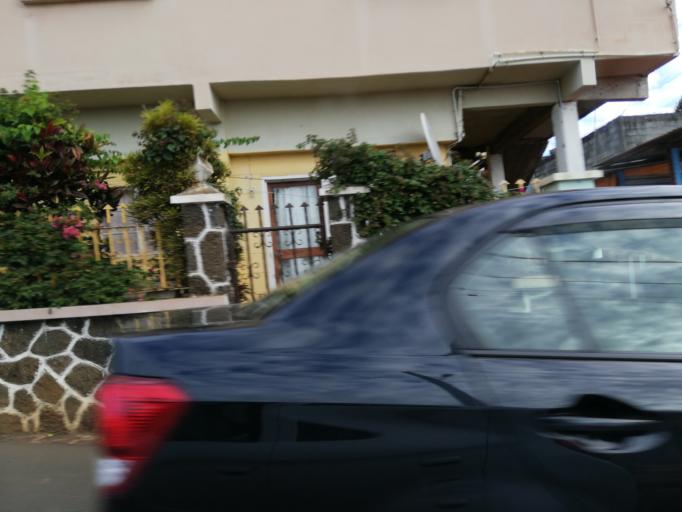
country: MU
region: Black River
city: Petite Riviere
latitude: -20.2212
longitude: 57.4594
